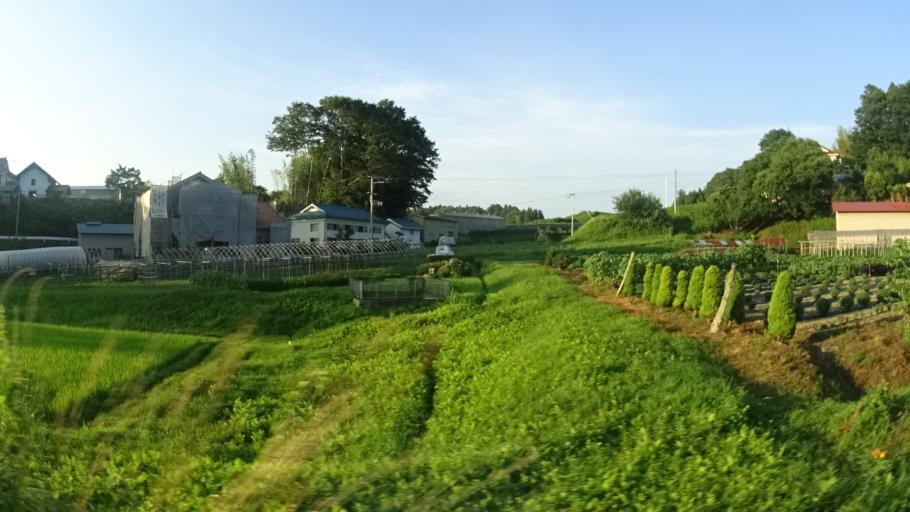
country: JP
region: Fukushima
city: Funehikimachi-funehiki
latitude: 37.4514
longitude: 140.5357
